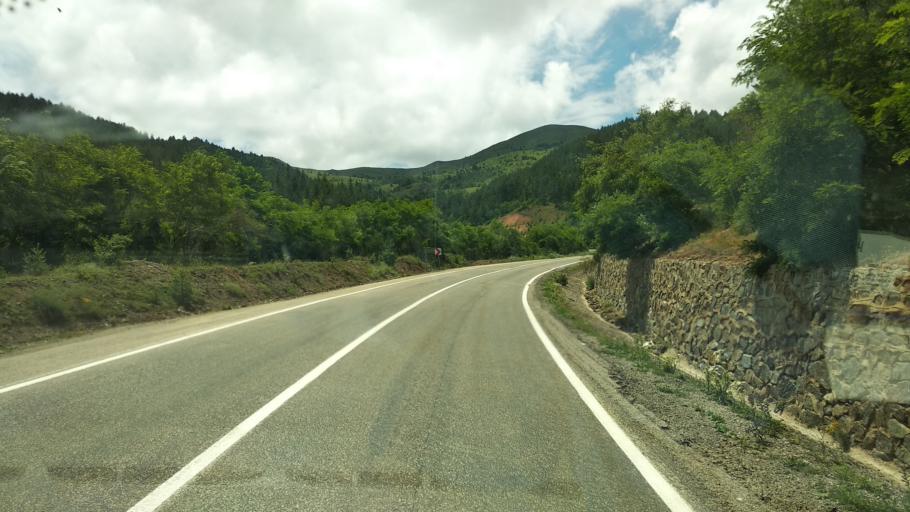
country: TR
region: Gumushane
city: Kose
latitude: 40.3003
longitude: 39.5565
